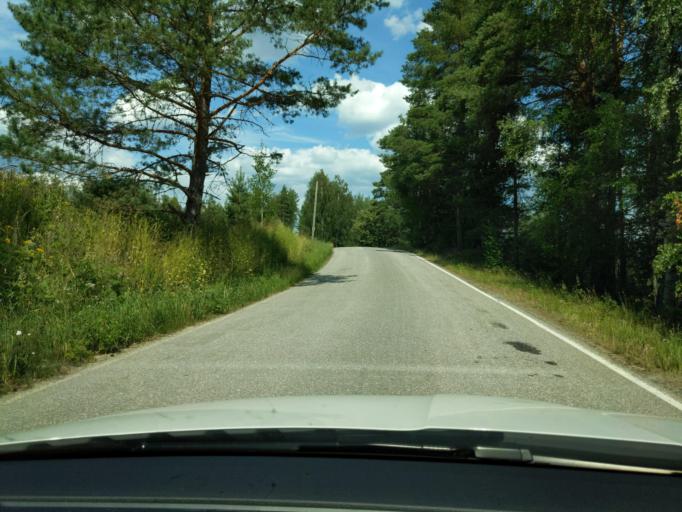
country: FI
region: Paijanne Tavastia
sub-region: Lahti
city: Heinola
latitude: 61.3396
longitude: 26.1741
